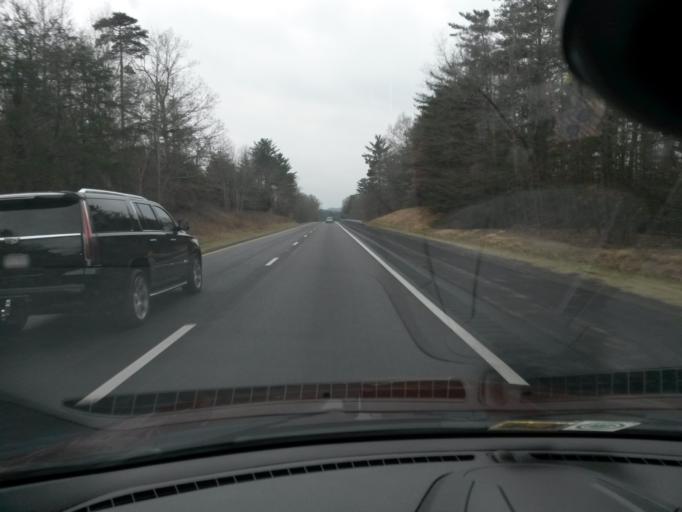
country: US
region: Virginia
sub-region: Alleghany County
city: Clifton Forge
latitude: 37.8218
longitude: -79.6640
